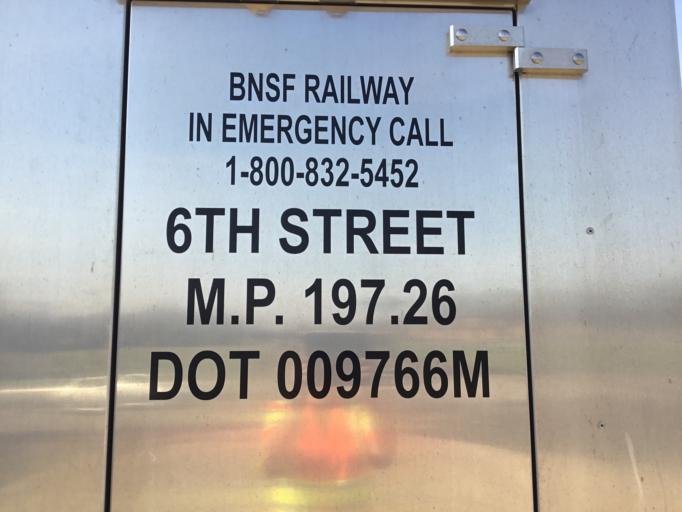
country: US
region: Kansas
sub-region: Butler County
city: Douglass
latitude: 37.5139
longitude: -97.0115
